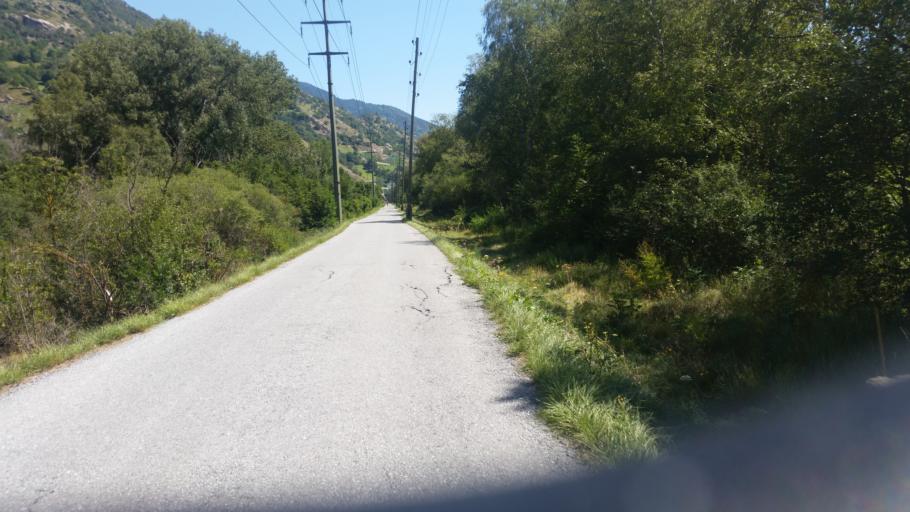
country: CH
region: Valais
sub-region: Raron District
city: Raron
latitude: 46.3078
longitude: 7.8160
